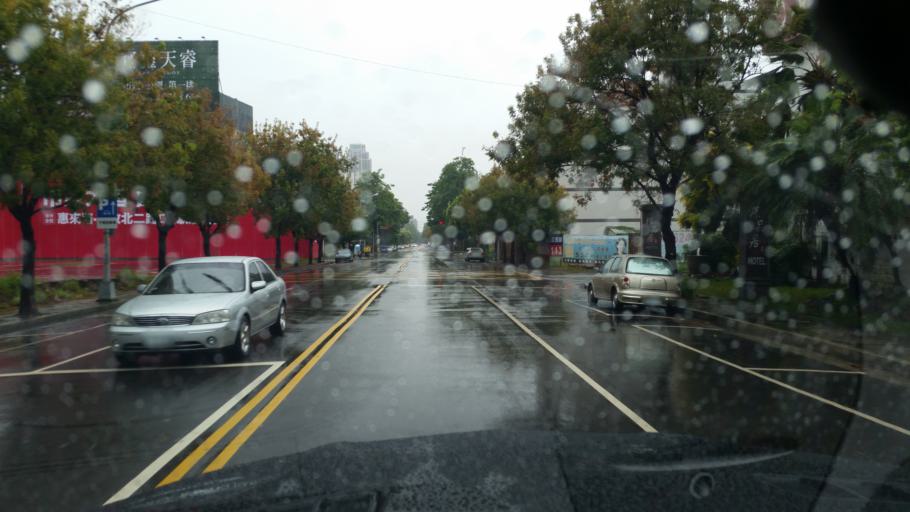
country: TW
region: Taiwan
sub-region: Taichung City
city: Taichung
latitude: 24.1559
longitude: 120.6440
